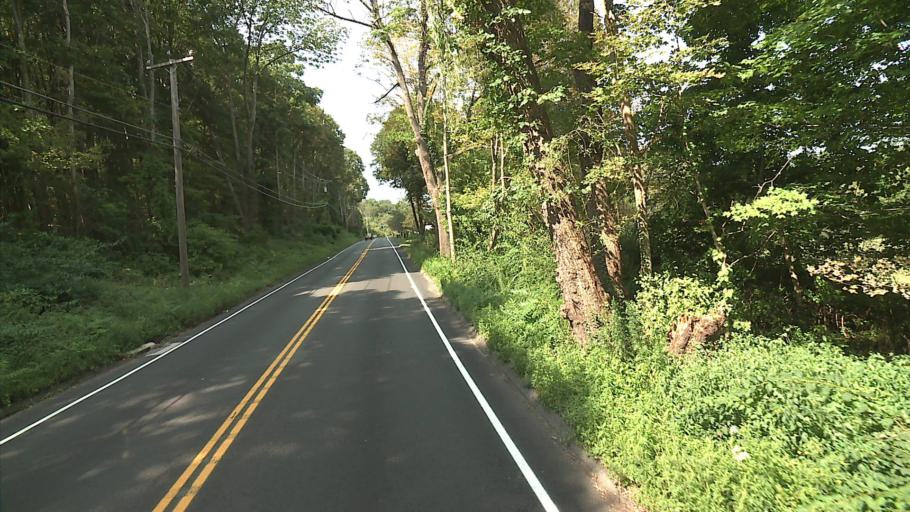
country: US
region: Connecticut
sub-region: Fairfield County
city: Bethel
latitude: 41.3645
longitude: -73.3871
